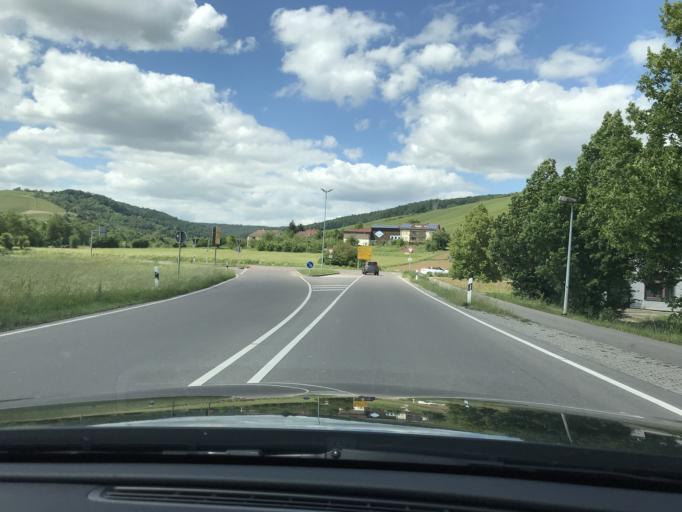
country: DE
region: Baden-Wuerttemberg
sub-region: Regierungsbezirk Stuttgart
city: Weinstadt-Endersbach
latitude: 48.8166
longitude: 9.4084
